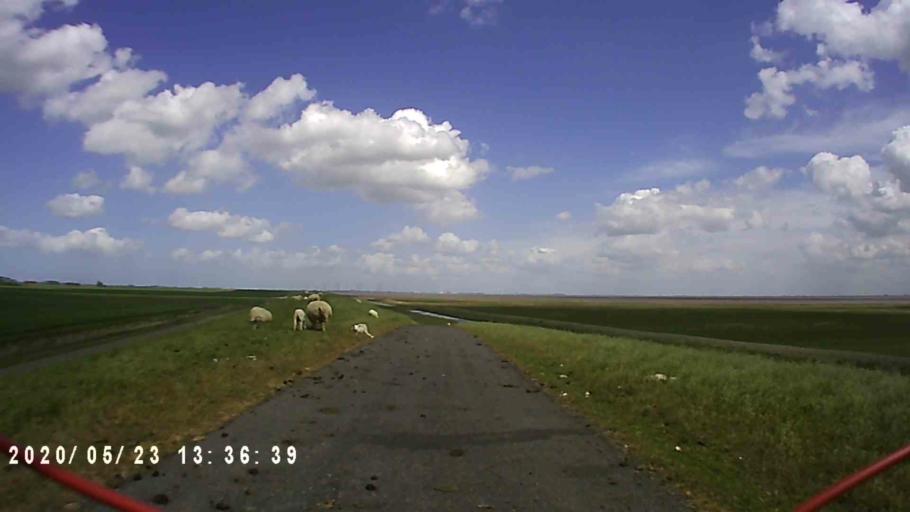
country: NL
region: Groningen
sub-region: Gemeente  Oldambt
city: Winschoten
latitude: 53.2655
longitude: 7.0710
